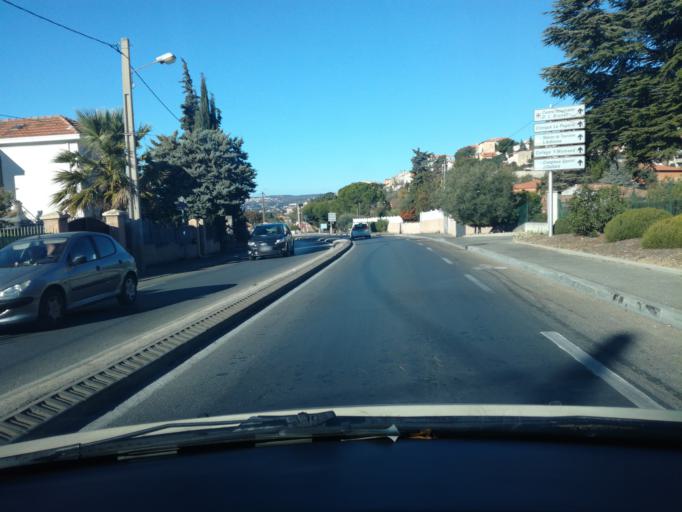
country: FR
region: Provence-Alpes-Cote d'Azur
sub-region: Departement des Bouches-du-Rhone
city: Allauch
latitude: 43.3314
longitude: 5.4881
